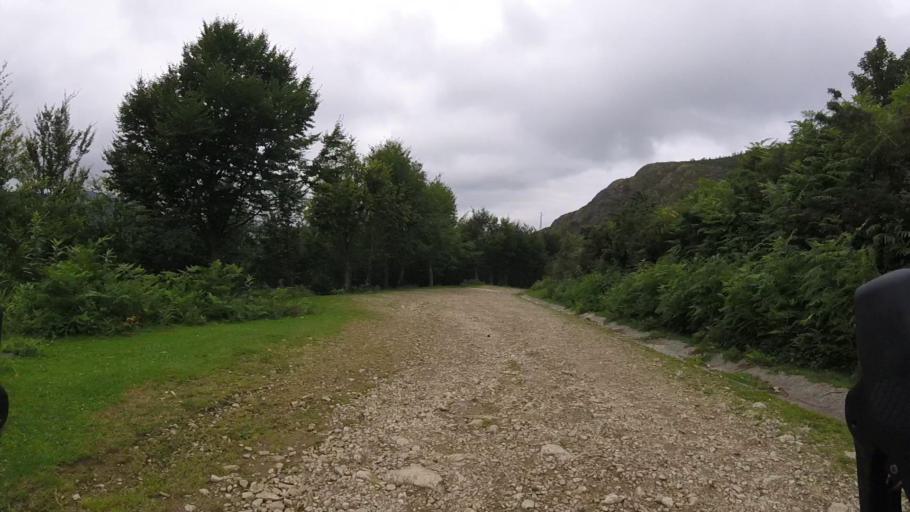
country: ES
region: Basque Country
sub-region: Provincia de Guipuzcoa
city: Irun
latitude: 43.2713
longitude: -1.7944
